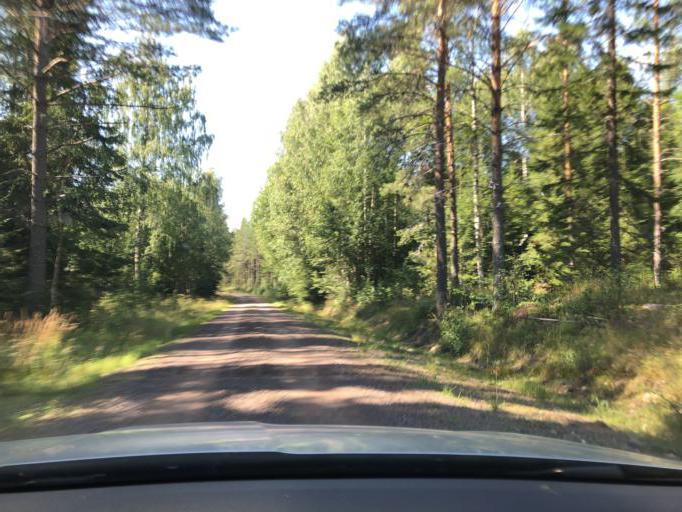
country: SE
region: Dalarna
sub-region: Orsa Kommun
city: Orsa
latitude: 61.2202
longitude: 14.7198
